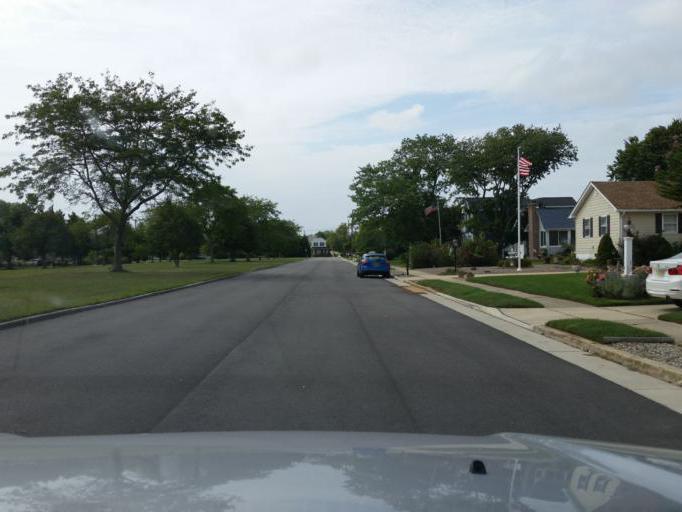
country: US
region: New Jersey
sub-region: Cape May County
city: Cape May
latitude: 38.9369
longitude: -74.9111
